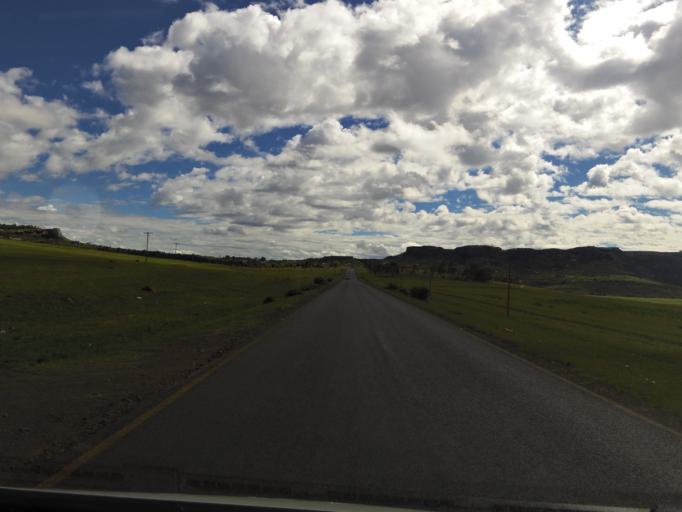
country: LS
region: Berea
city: Teyateyaneng
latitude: -28.9934
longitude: 27.7588
